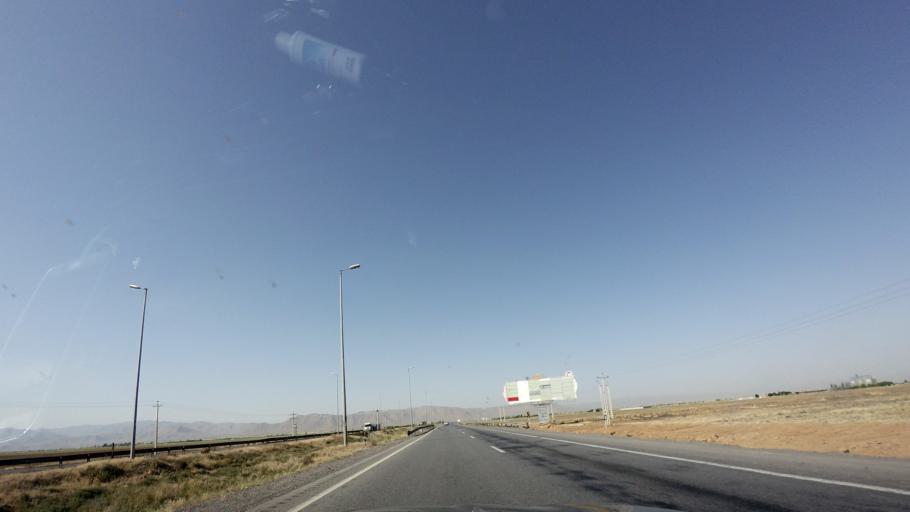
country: IR
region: Markazi
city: Ashtian
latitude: 34.1952
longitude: 50.0571
